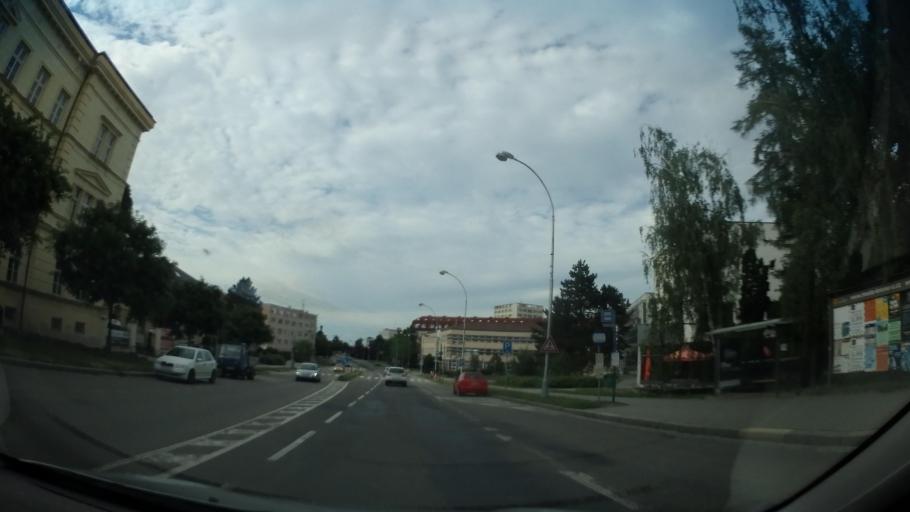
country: CZ
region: Zlin
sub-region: Okres Kromeriz
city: Kromeriz
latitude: 49.2979
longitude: 17.3984
